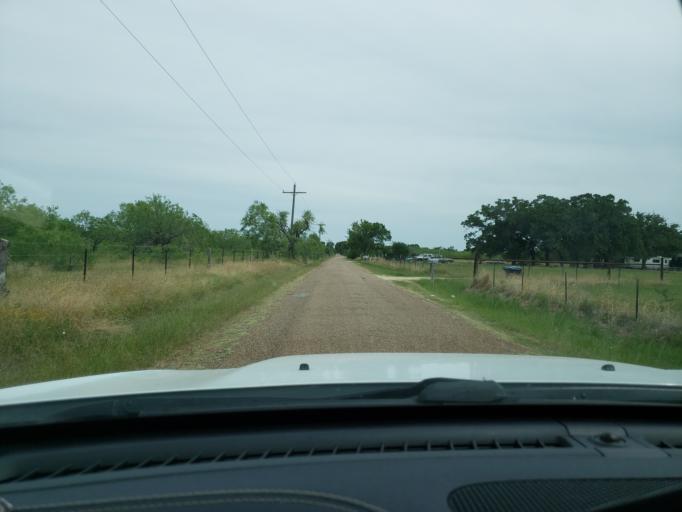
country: US
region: Texas
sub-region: Burleson County
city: Somerville
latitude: 30.3556
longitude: -96.5484
